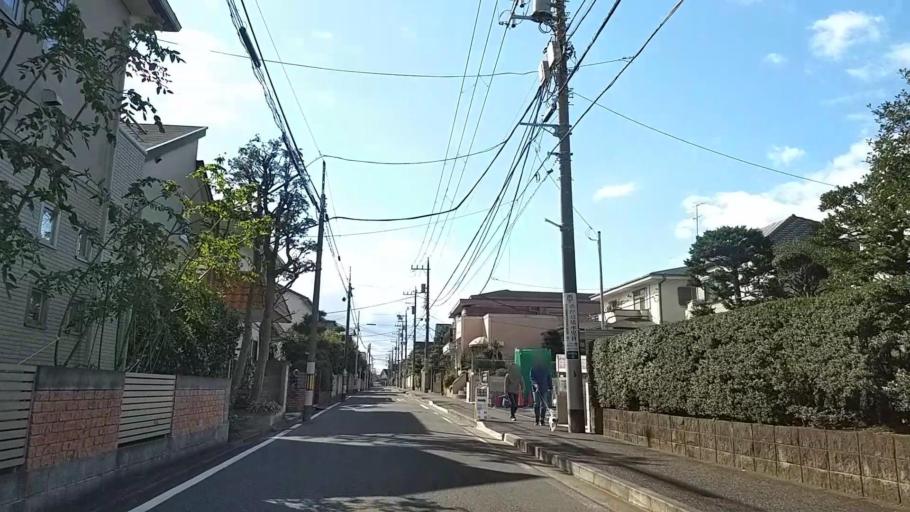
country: JP
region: Kanagawa
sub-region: Kawasaki-shi
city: Kawasaki
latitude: 35.5128
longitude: 139.6660
